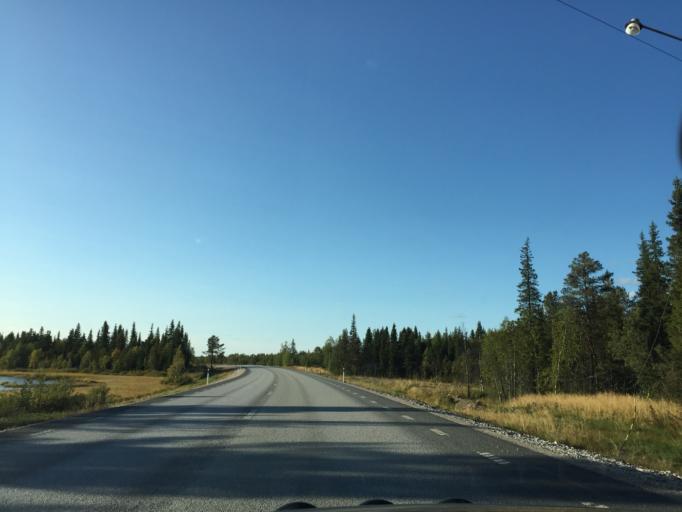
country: SE
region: Norrbotten
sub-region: Gallivare Kommun
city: Malmberget
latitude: 67.6402
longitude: 21.0609
